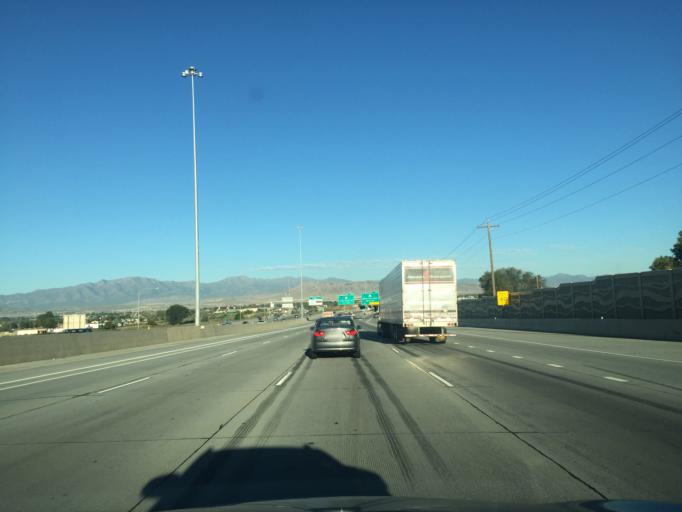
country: US
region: Utah
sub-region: Utah County
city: American Fork
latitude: 40.3737
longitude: -111.8092
